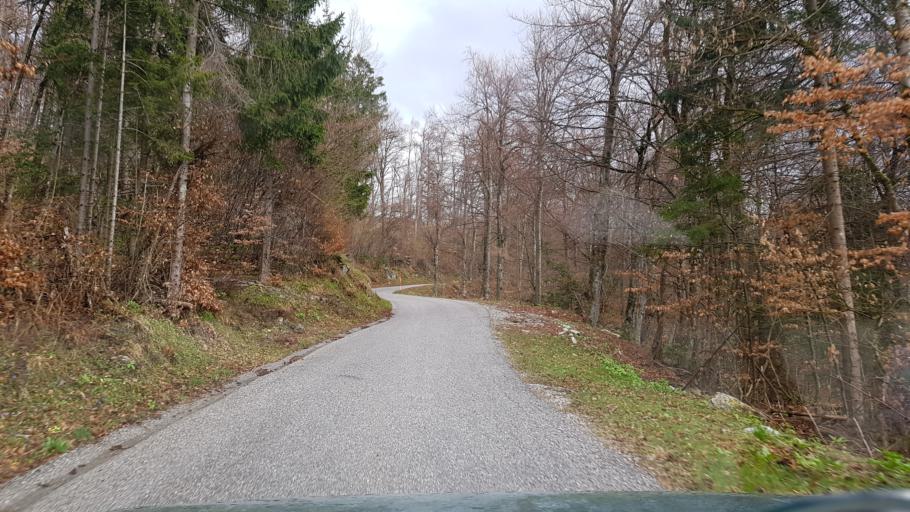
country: SI
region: Cerkno
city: Cerkno
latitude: 46.1299
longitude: 13.8700
